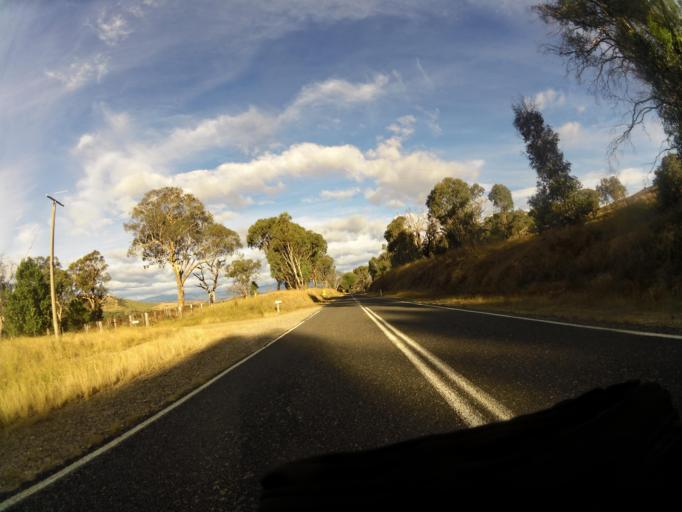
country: AU
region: New South Wales
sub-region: Greater Hume Shire
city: Holbrook
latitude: -36.0088
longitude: 147.9057
